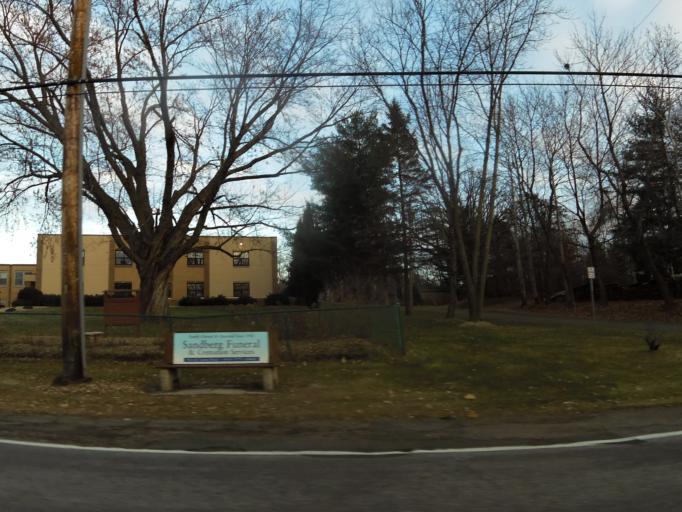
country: US
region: Minnesota
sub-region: Washington County
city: Mahtomedi
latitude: 45.0632
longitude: -92.9581
